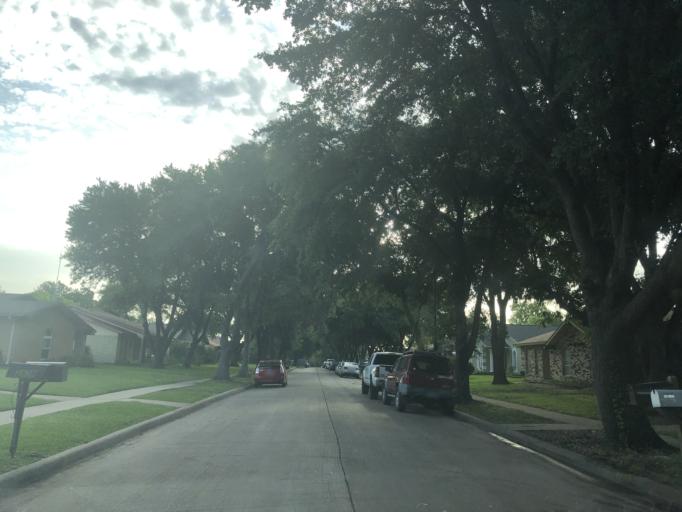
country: US
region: Texas
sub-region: Dallas County
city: Sunnyvale
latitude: 32.8404
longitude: -96.5866
